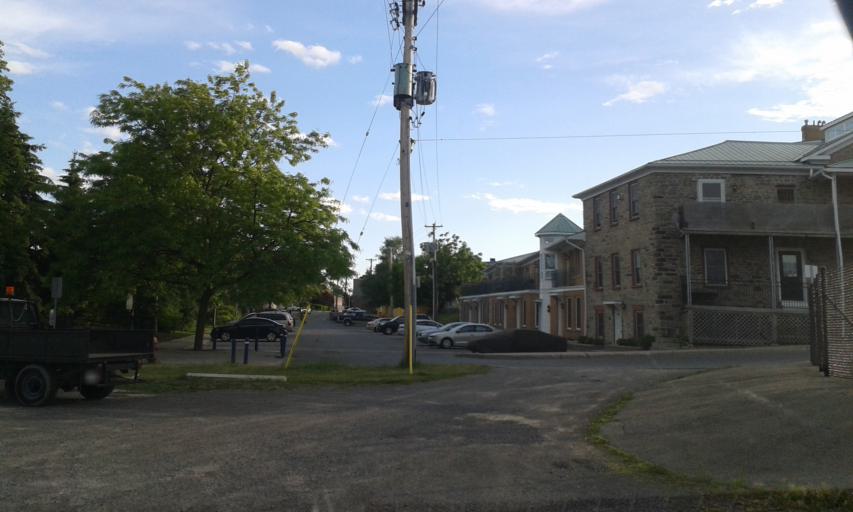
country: CA
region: Ontario
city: Prescott
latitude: 44.7111
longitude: -75.5110
